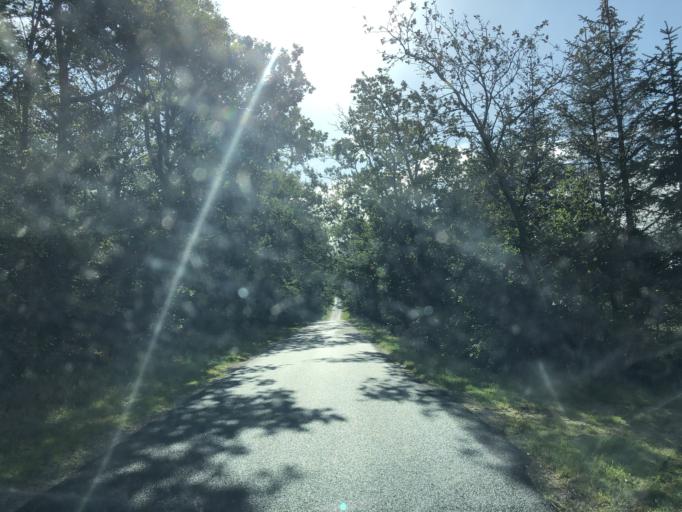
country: DK
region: Central Jutland
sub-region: Holstebro Kommune
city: Ulfborg
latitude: 56.2954
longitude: 8.4614
